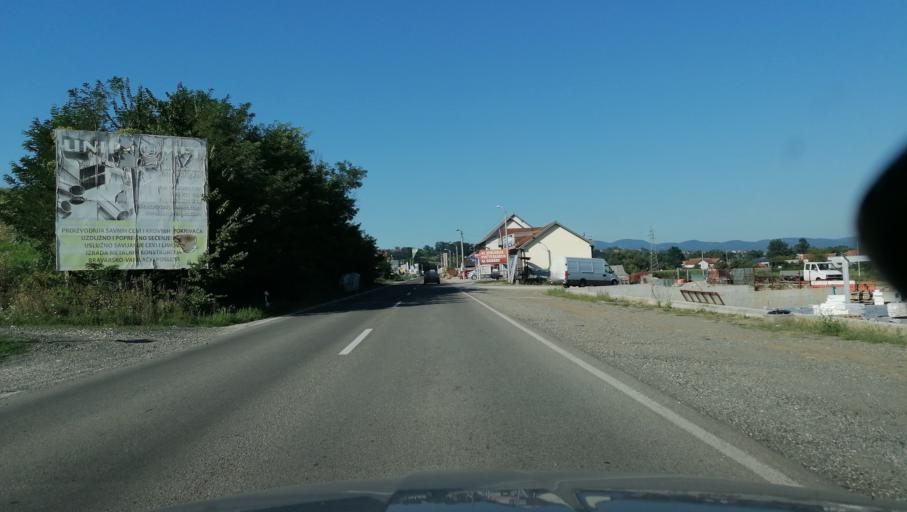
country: RS
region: Central Serbia
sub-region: Raski Okrug
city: Kraljevo
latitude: 43.7083
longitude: 20.6154
